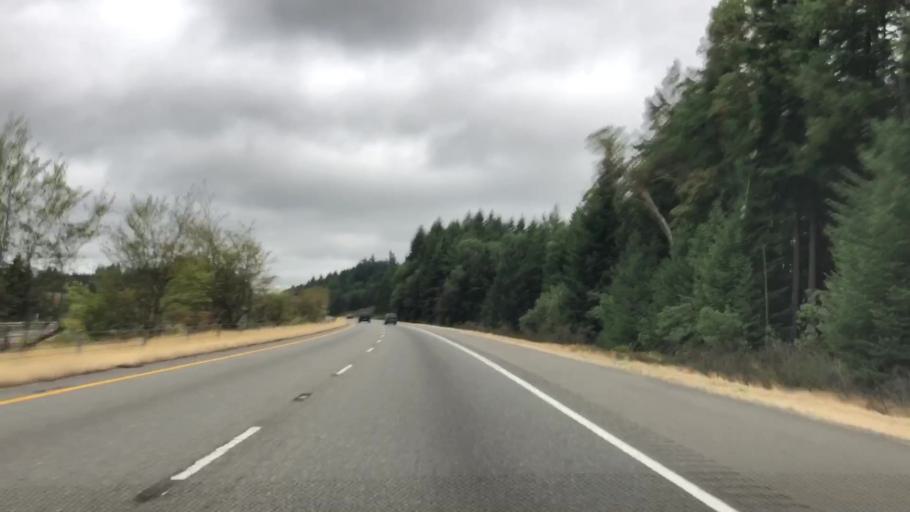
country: US
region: Washington
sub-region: Pierce County
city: Purdy
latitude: 47.3777
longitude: -122.6158
